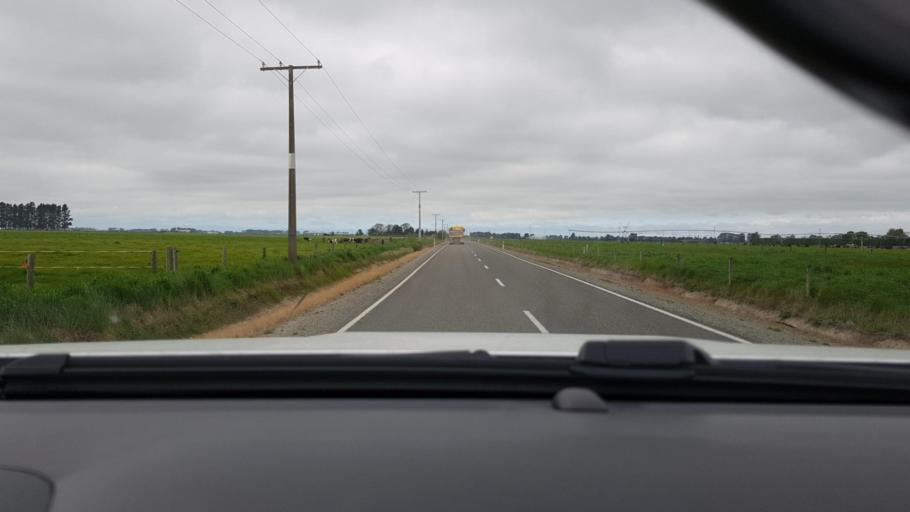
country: NZ
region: Otago
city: Oamaru
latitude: -44.9648
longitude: 170.9662
